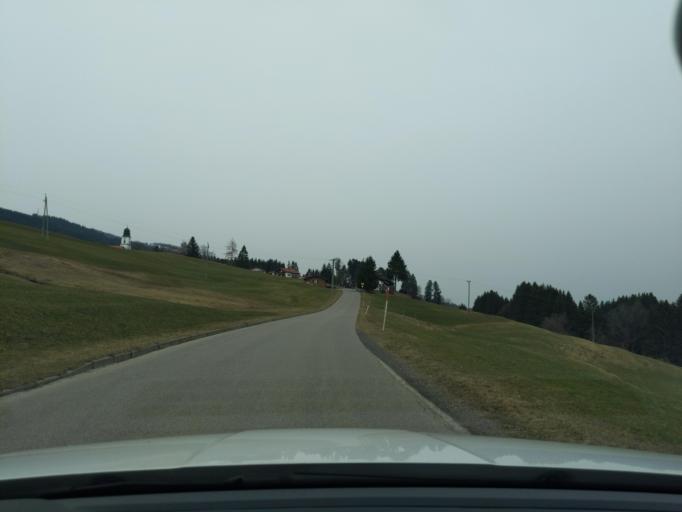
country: DE
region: Bavaria
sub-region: Swabia
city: Ofterschwang
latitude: 47.4924
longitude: 10.2407
